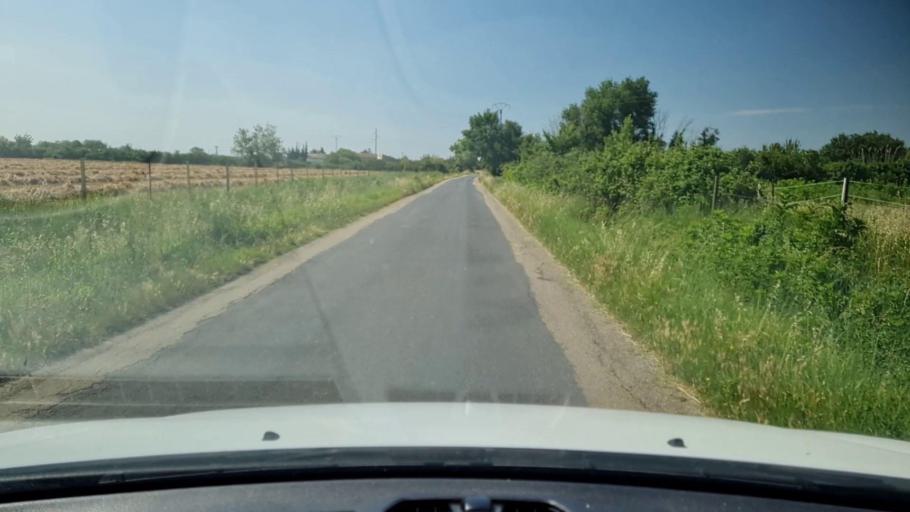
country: FR
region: Languedoc-Roussillon
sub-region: Departement du Gard
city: Le Cailar
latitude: 43.6653
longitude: 4.2315
